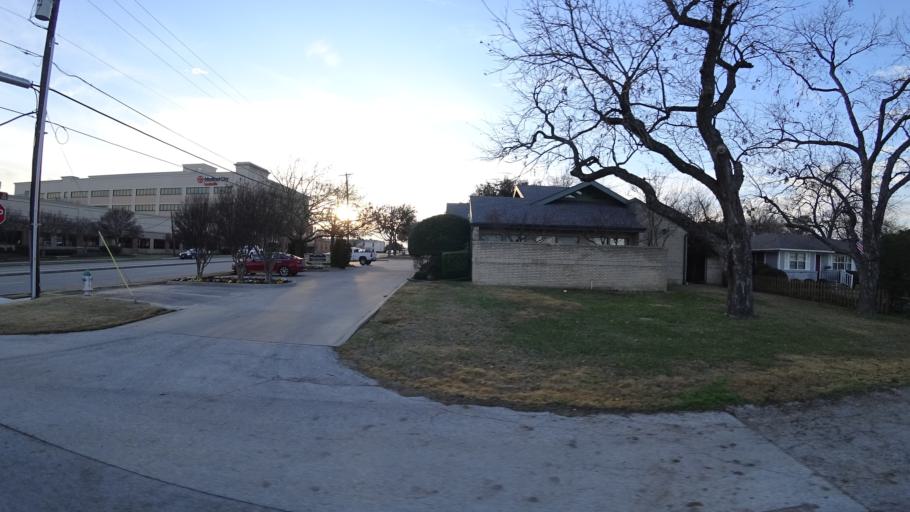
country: US
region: Texas
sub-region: Denton County
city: Lewisville
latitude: 33.0466
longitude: -97.0042
